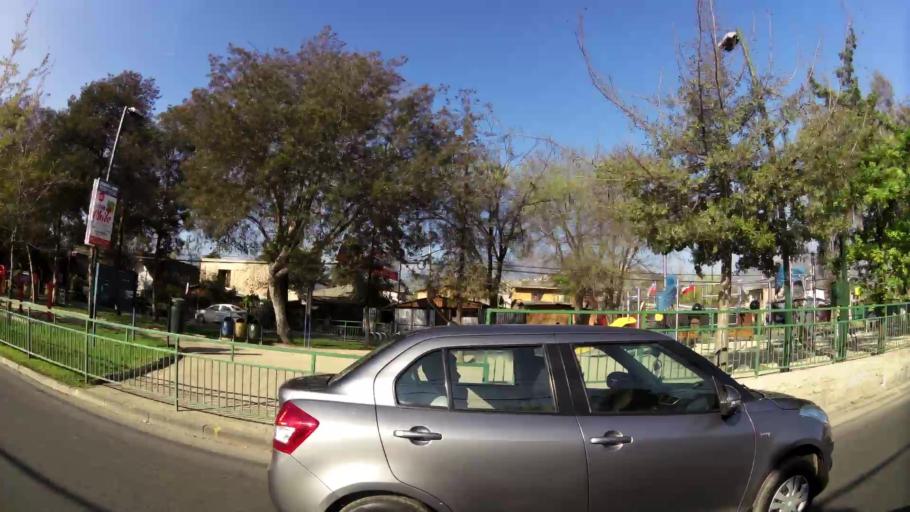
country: CL
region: Santiago Metropolitan
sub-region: Provincia de Santiago
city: Villa Presidente Frei, Nunoa, Santiago, Chile
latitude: -33.3596
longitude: -70.5097
